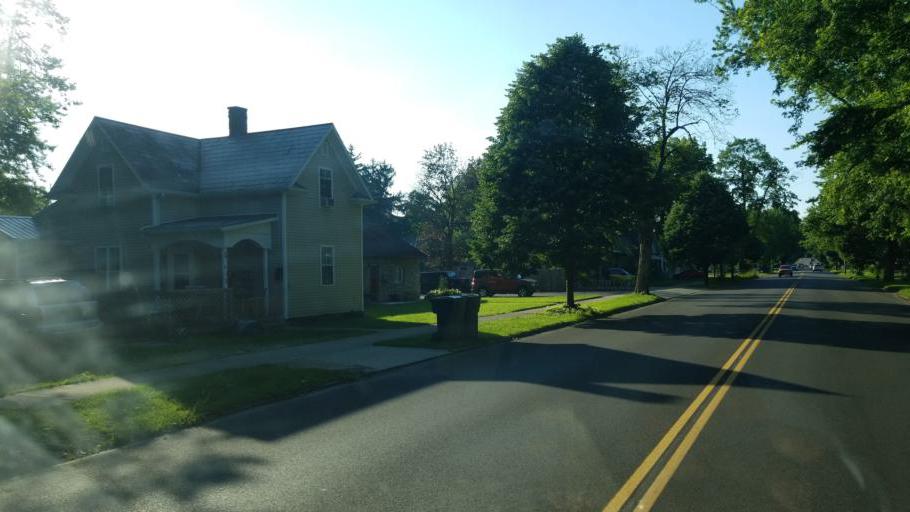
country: US
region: Ohio
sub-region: Knox County
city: Mount Vernon
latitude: 40.4008
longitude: -82.4906
